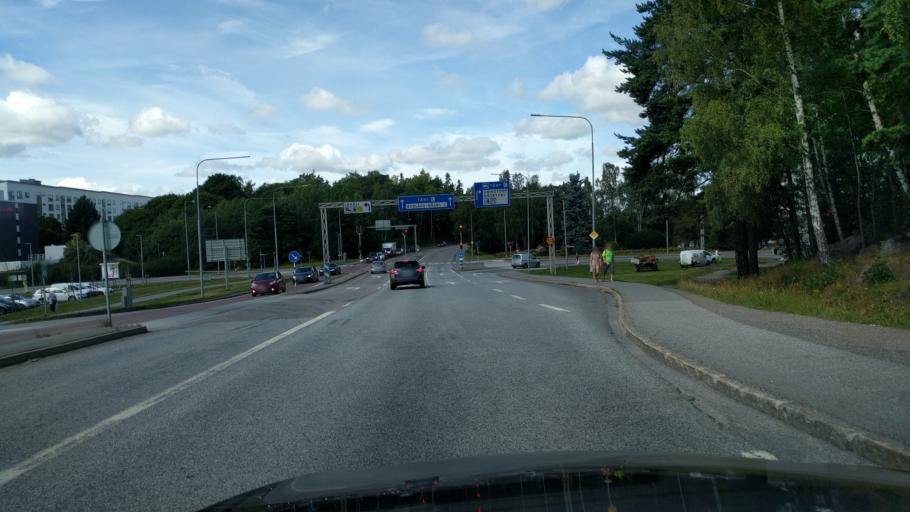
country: SE
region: Stockholm
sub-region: Taby Kommun
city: Taby
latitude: 59.4348
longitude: 18.0680
